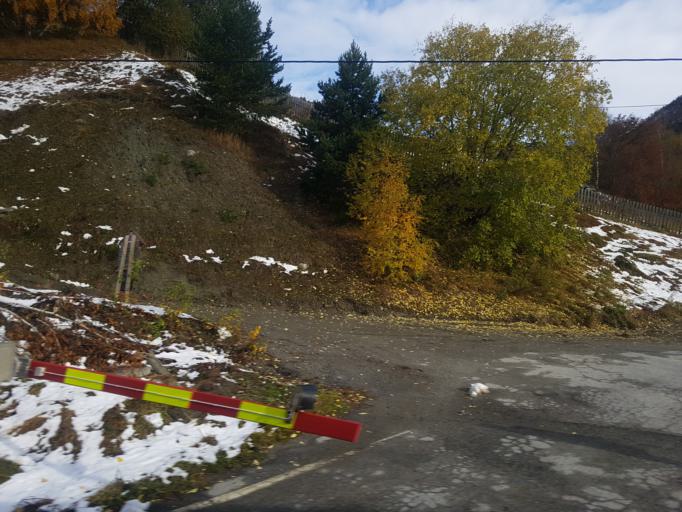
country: NO
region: Oppland
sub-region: Dovre
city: Dombas
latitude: 62.0461
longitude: 9.1448
